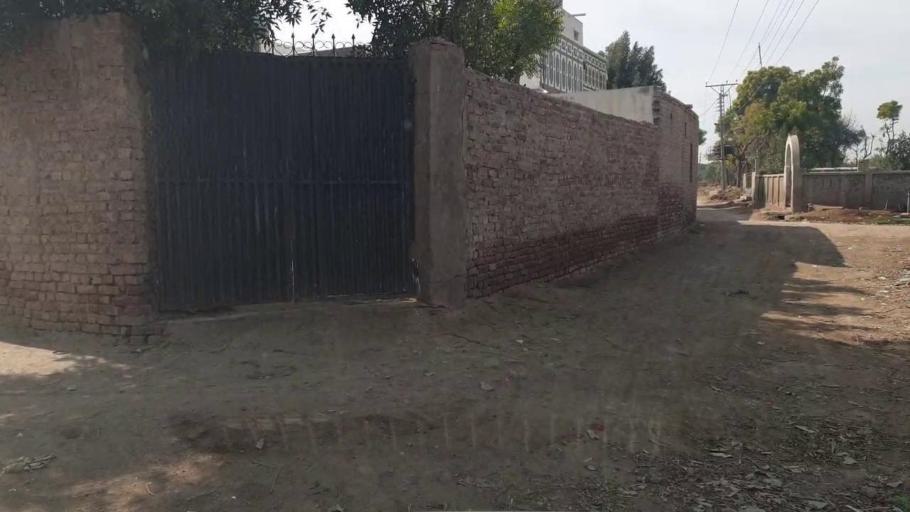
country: PK
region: Sindh
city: Sakrand
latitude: 25.9922
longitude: 68.3727
